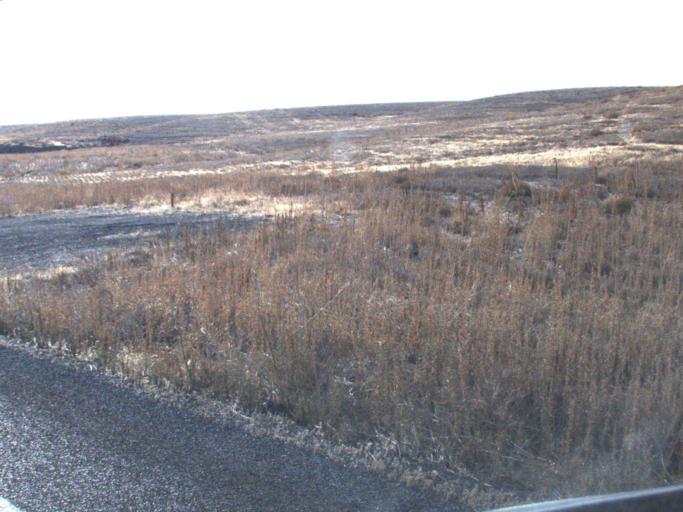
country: US
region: Washington
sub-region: Franklin County
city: Connell
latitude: 46.6341
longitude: -118.7605
